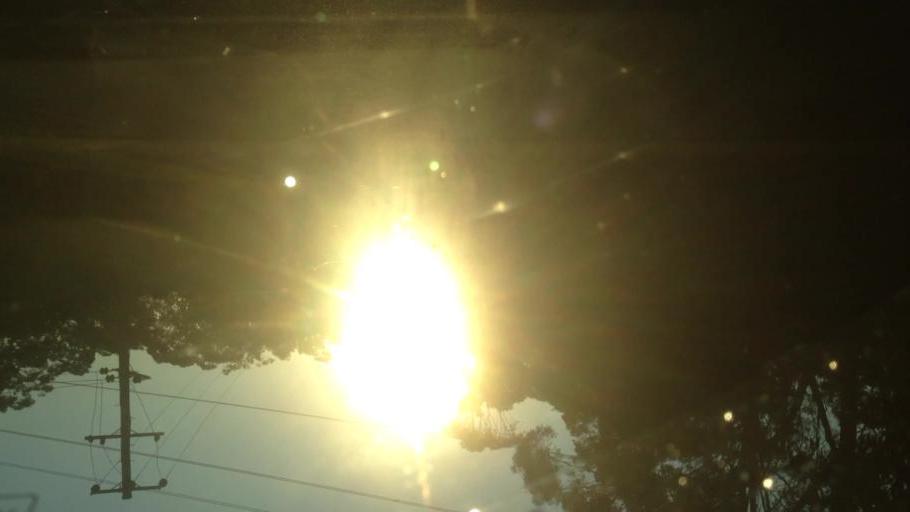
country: AU
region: New South Wales
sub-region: Wyong Shire
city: Kingfisher Shores
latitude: -33.1533
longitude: 151.5147
